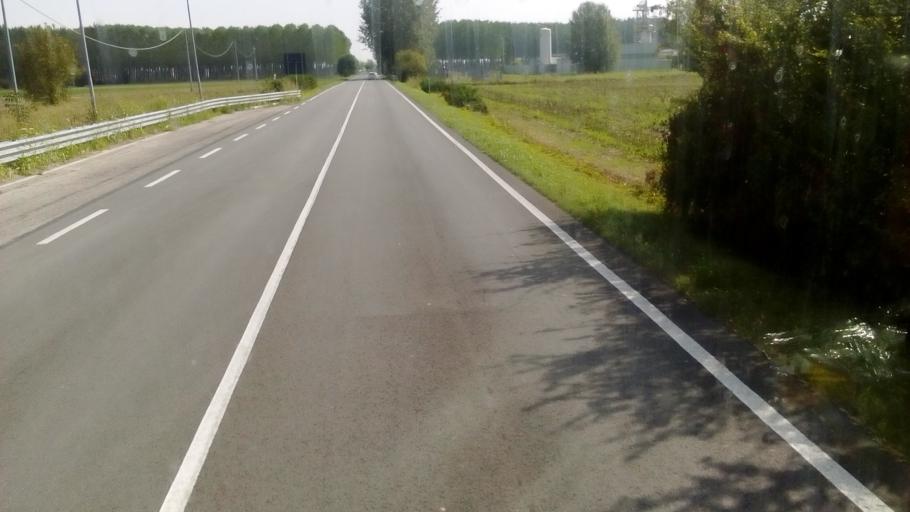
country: IT
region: Veneto
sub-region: Provincia di Rovigo
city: Castelmassa
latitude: 45.0274
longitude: 11.3137
